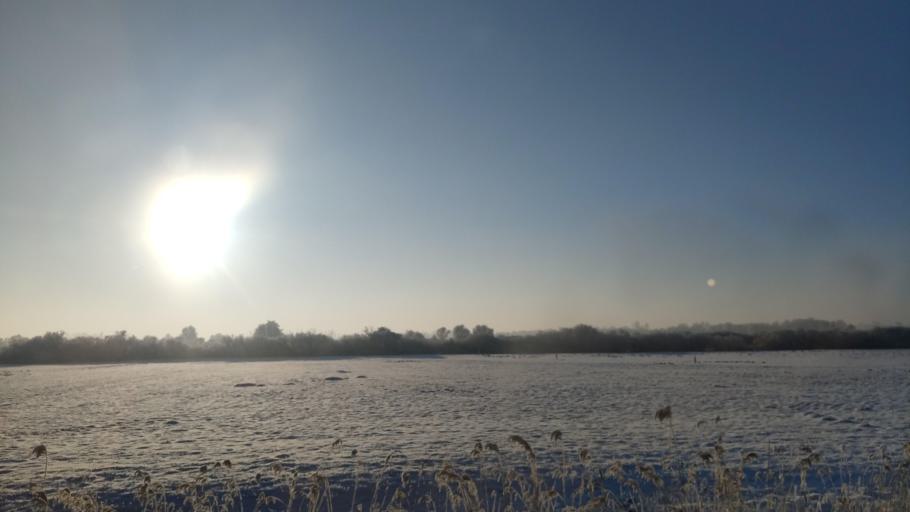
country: PL
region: Kujawsko-Pomorskie
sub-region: Powiat zninski
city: Barcin
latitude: 52.8761
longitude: 17.8697
